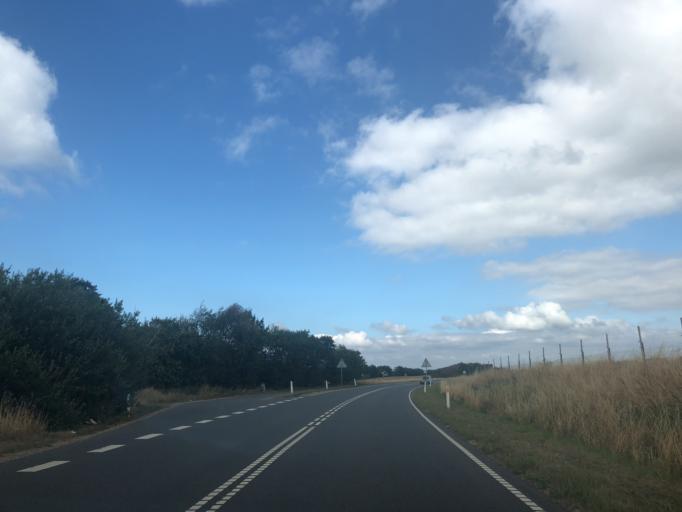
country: DK
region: Central Jutland
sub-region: Holstebro Kommune
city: Vinderup
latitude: 56.4689
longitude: 8.7051
